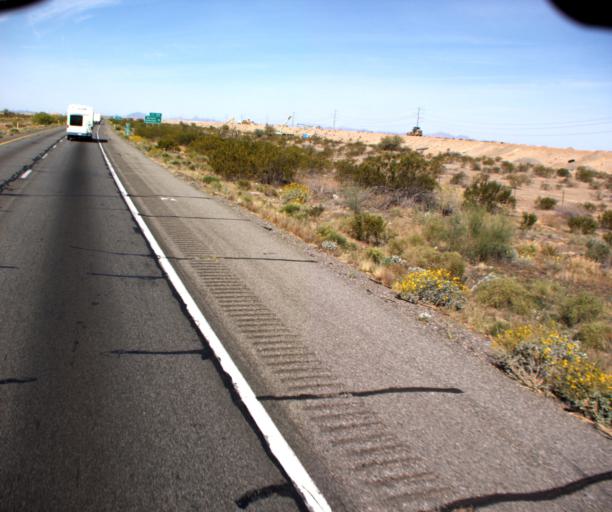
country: US
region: Arizona
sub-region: Maricopa County
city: Buckeye
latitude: 33.4350
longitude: -112.6577
